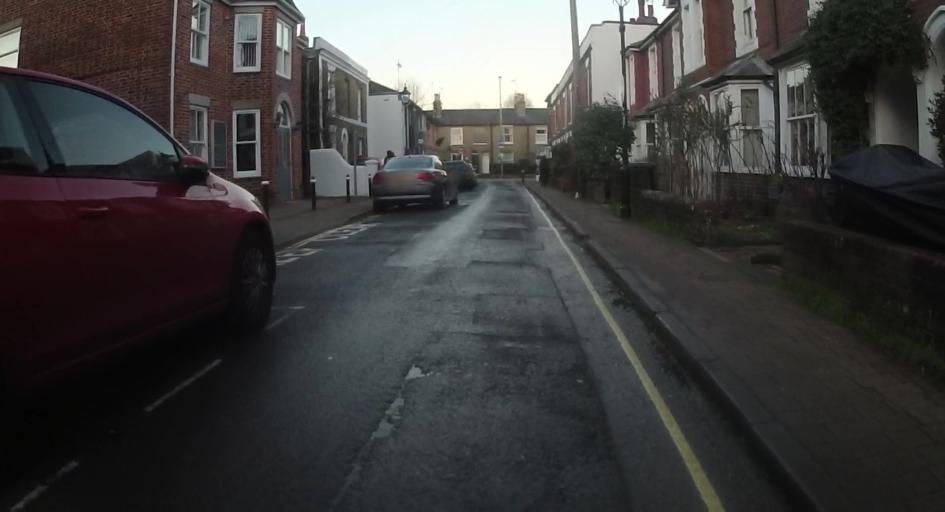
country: GB
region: England
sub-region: Hampshire
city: Winchester
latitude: 51.0649
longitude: -1.3130
